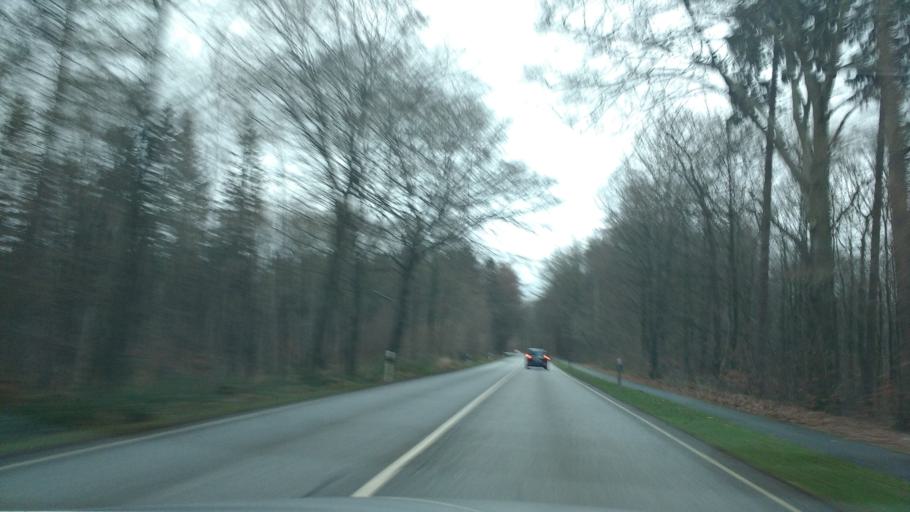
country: DE
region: Schleswig-Holstein
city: Oelixdorf
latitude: 53.9433
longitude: 9.5405
